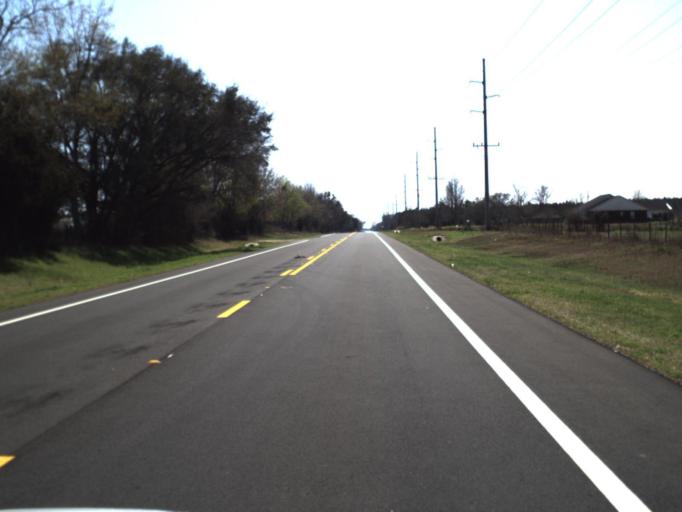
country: US
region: Florida
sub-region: Jackson County
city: Sneads
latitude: 30.7713
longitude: -85.0192
